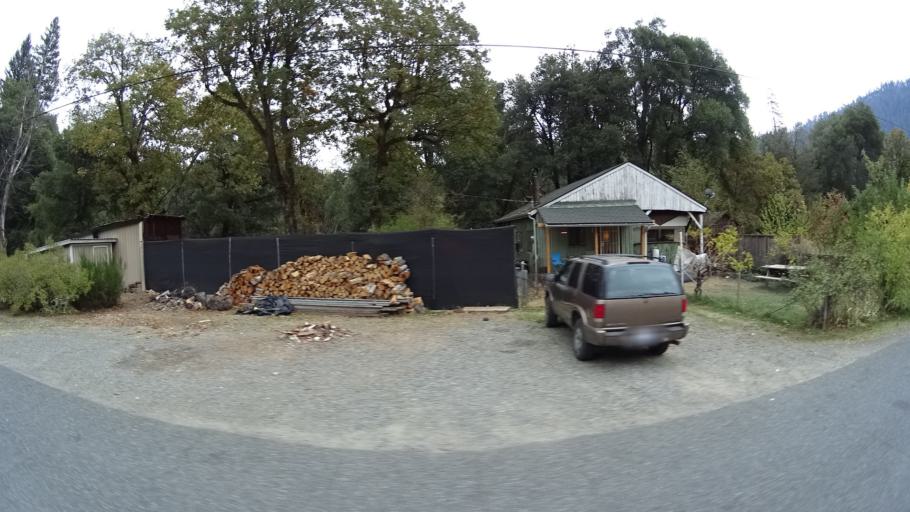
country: US
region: California
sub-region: Siskiyou County
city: Happy Camp
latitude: 41.7983
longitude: -123.3798
